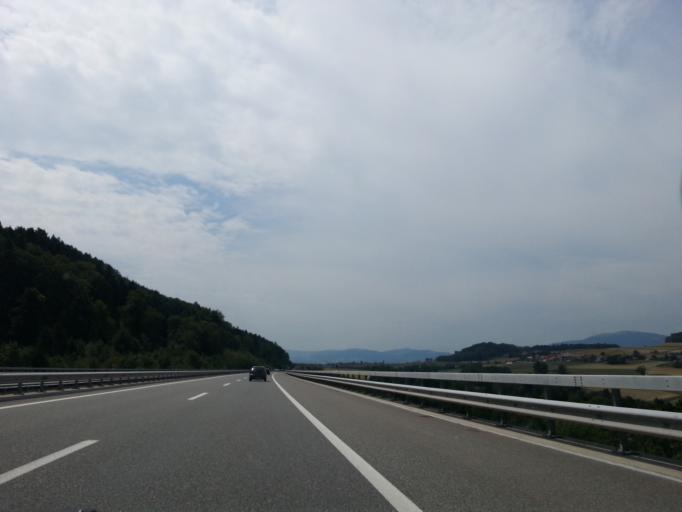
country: CH
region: Vaud
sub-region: Jura-Nord vaudois District
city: Yvonand
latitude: 46.7716
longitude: 6.7115
